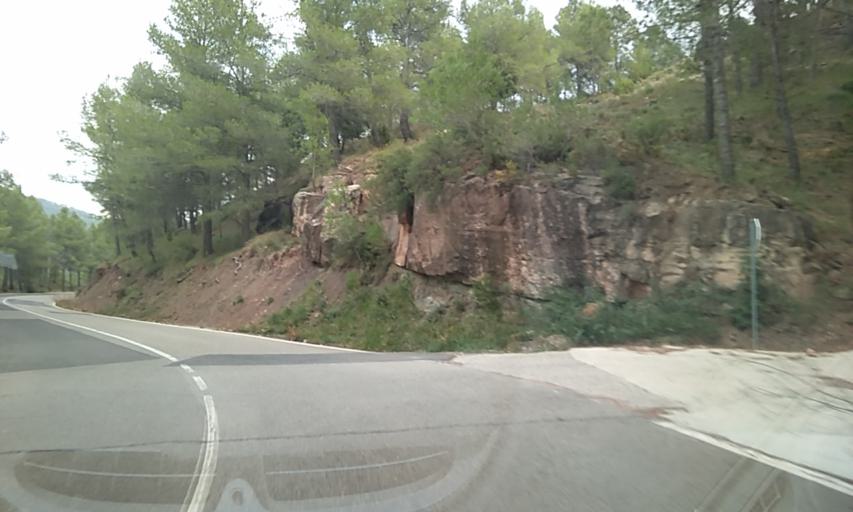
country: ES
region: Valencia
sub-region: Provincia de Castello
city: Puebla de Arenoso
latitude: 40.0875
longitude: -0.5597
